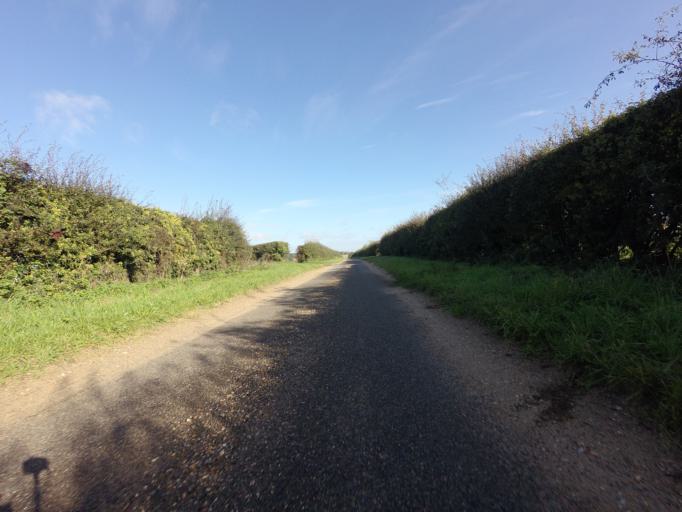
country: GB
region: England
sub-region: Norfolk
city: Dersingham
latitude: 52.8323
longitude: 0.6748
